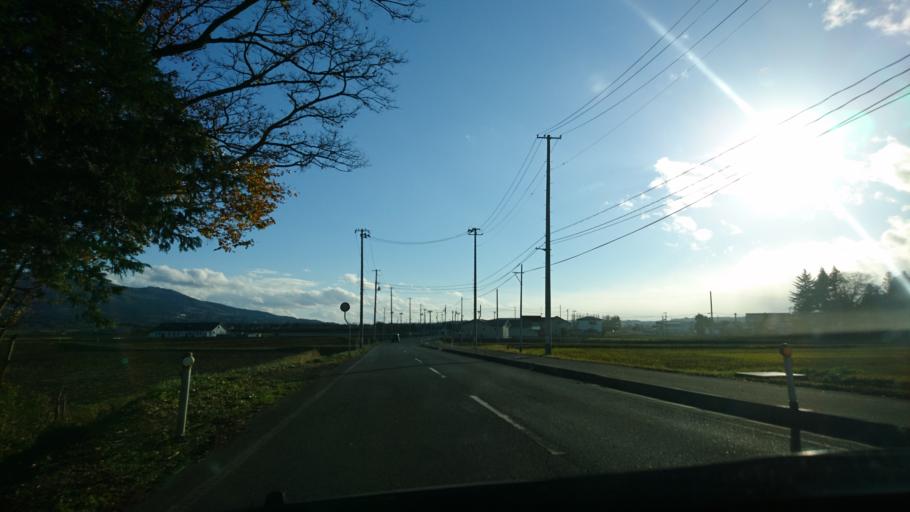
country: JP
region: Iwate
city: Mizusawa
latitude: 39.0628
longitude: 141.1438
